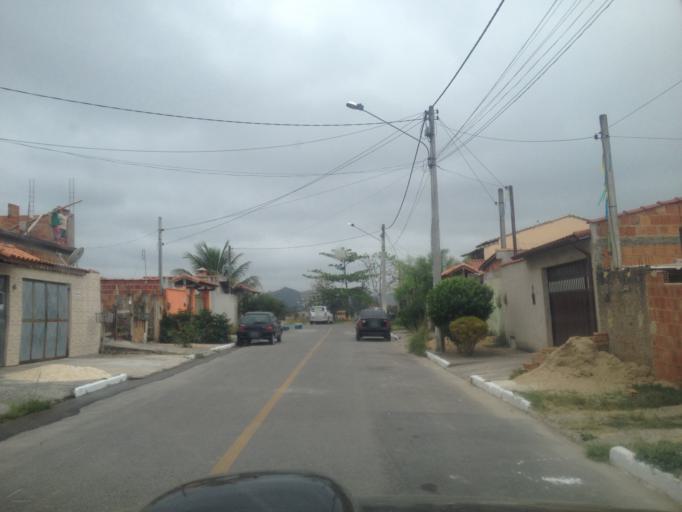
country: BR
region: Rio de Janeiro
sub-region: Porto Real
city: Porto Real
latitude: -22.4124
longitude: -44.3068
